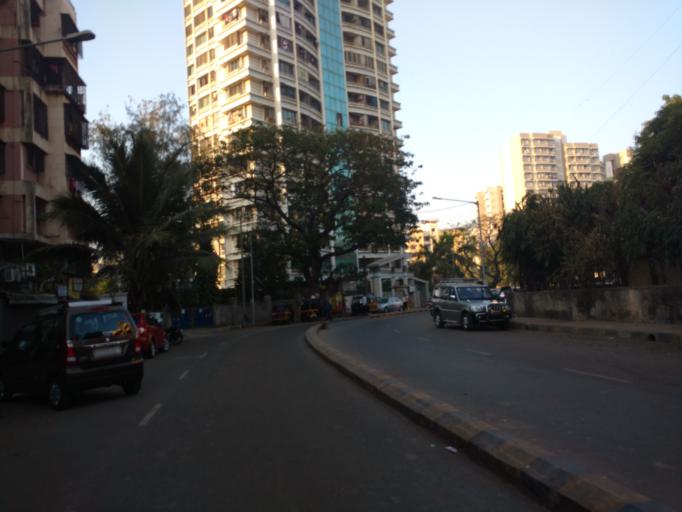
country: IN
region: Maharashtra
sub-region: Mumbai Suburban
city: Borivli
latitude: 19.2057
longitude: 72.8378
